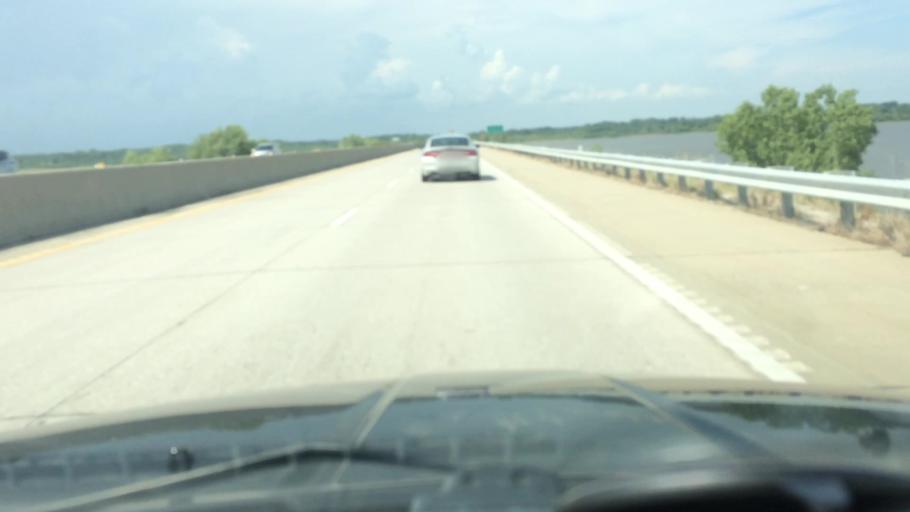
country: US
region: Missouri
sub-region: Henry County
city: Clinton
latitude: 38.2741
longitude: -93.7598
